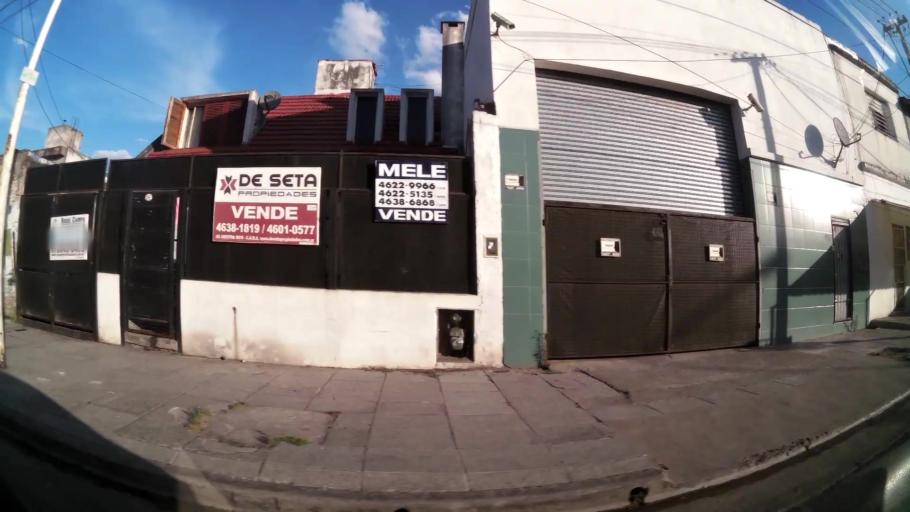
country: AR
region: Buenos Aires F.D.
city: Villa Lugano
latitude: -34.6892
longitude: -58.4854
